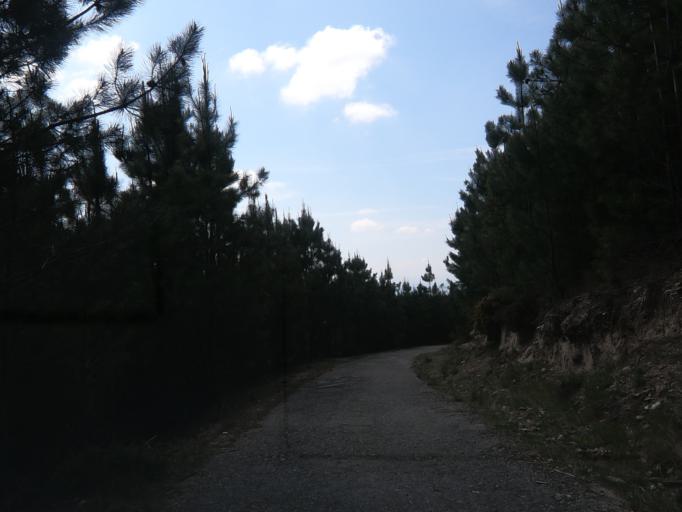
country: PT
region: Vila Real
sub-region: Vila Real
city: Vila Real
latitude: 41.3622
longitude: -7.7371
